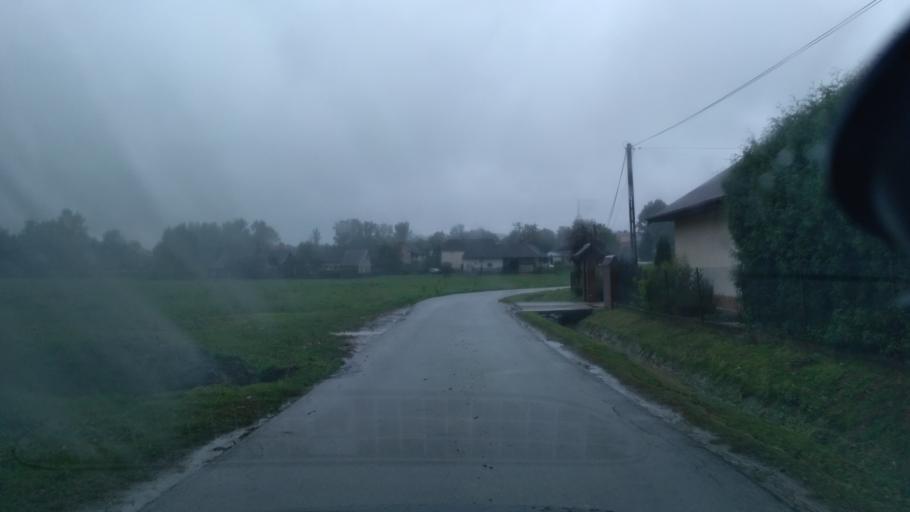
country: PL
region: Subcarpathian Voivodeship
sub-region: Powiat ropczycko-sedziszowski
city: Niedzwiada
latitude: 50.0276
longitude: 21.5418
